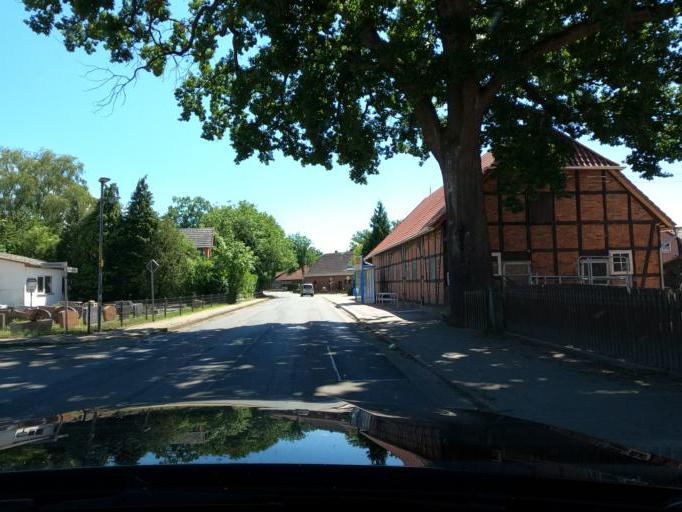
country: DE
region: Lower Saxony
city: Muden
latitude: 52.5281
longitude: 10.3558
